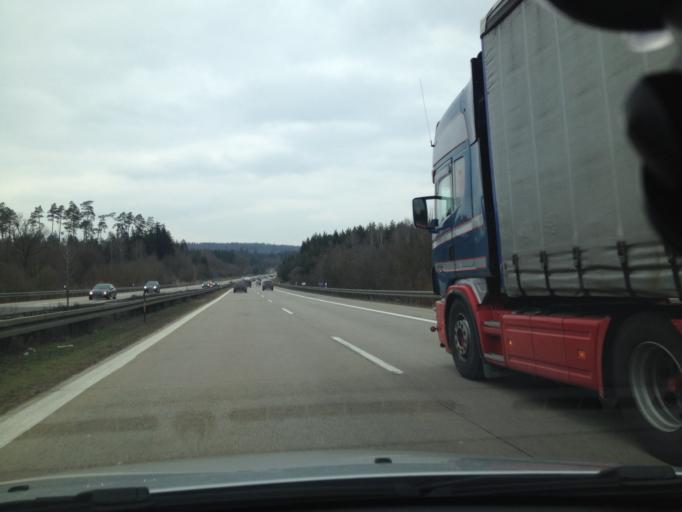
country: DE
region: Baden-Wuerttemberg
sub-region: Regierungsbezirk Stuttgart
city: Ellenberg
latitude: 48.9947
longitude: 10.1946
